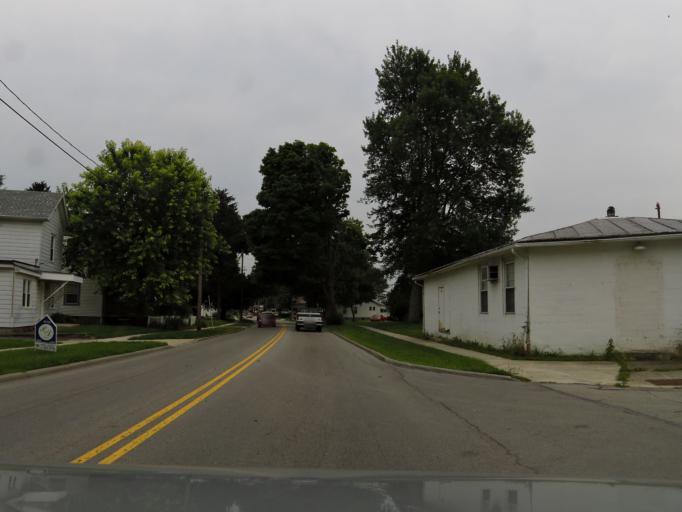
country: US
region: Ohio
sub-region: Clinton County
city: Wilmington
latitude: 39.4551
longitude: -83.8308
